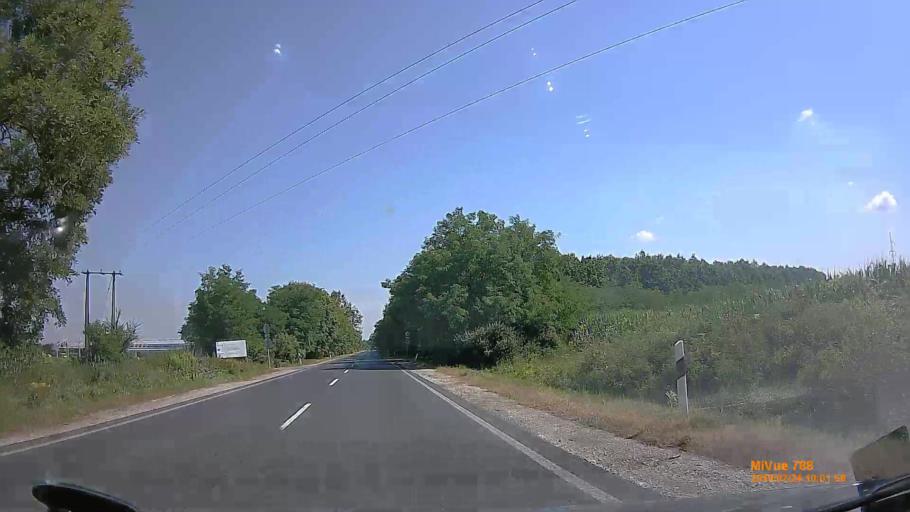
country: HU
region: Szabolcs-Szatmar-Bereg
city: Vasarosnameny
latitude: 48.1062
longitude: 22.3014
